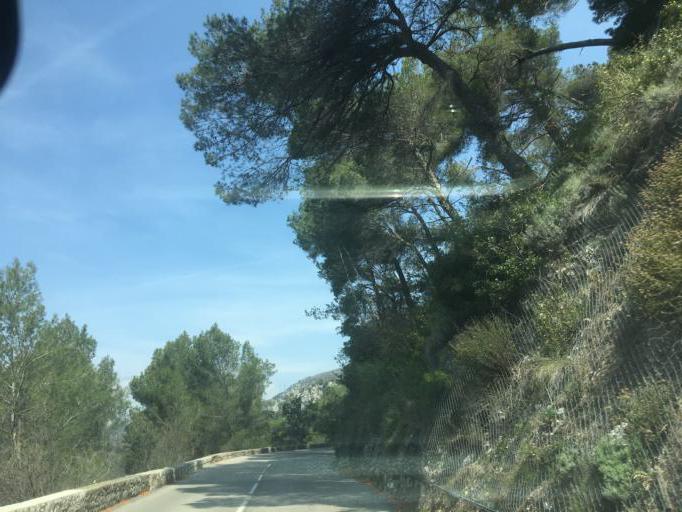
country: FR
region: Provence-Alpes-Cote d'Azur
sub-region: Departement des Alpes-Maritimes
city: Saint-Martin-du-Var
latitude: 43.8268
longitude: 7.1931
